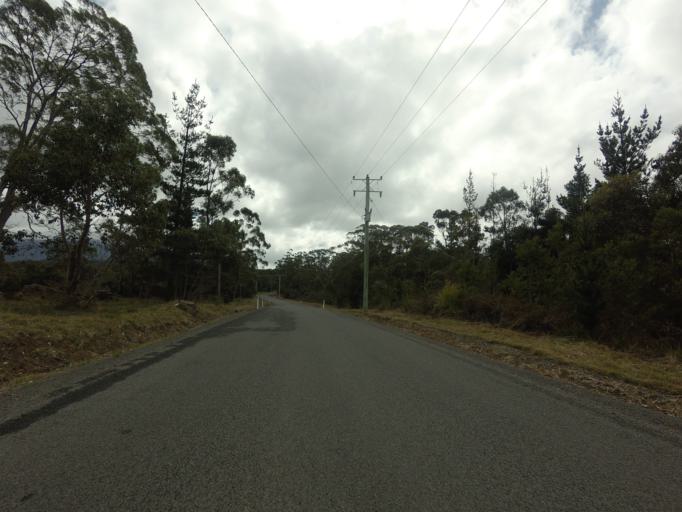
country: AU
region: Tasmania
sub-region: Huon Valley
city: Geeveston
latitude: -43.4348
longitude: 146.9037
